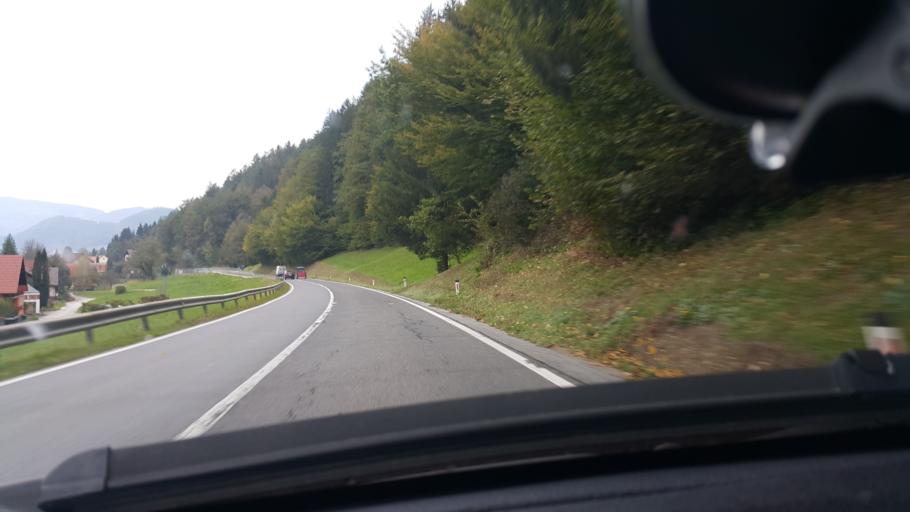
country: SI
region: Radlje ob Dravi
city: Radlje ob Dravi
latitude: 46.5960
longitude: 15.2680
